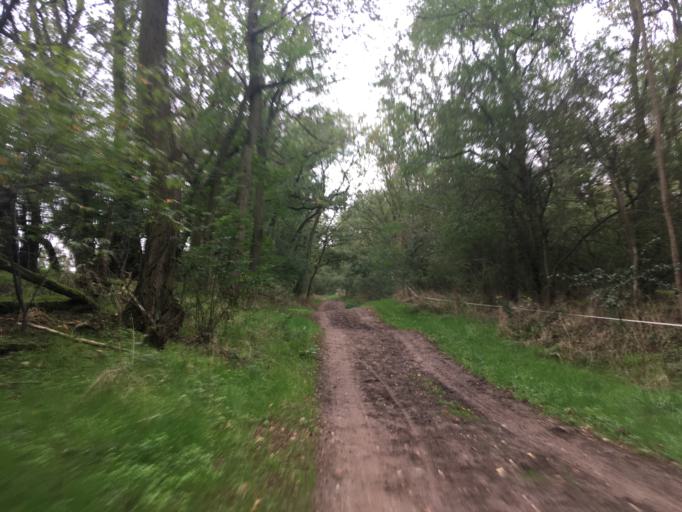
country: DE
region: Brandenburg
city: Falkensee
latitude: 52.5086
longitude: 13.0989
